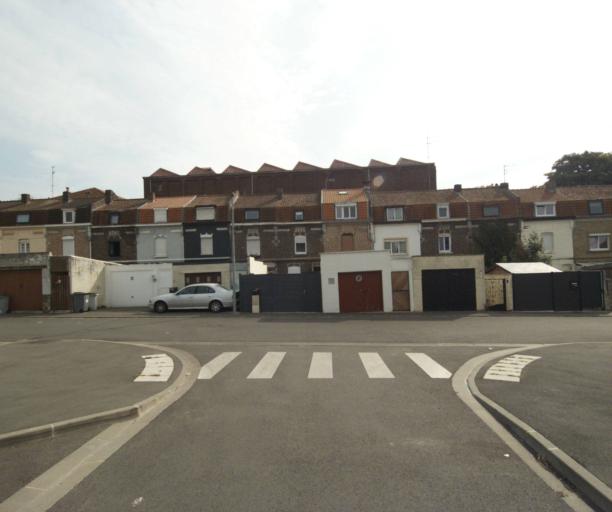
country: FR
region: Nord-Pas-de-Calais
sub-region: Departement du Nord
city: Haubourdin
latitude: 50.6043
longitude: 2.9875
